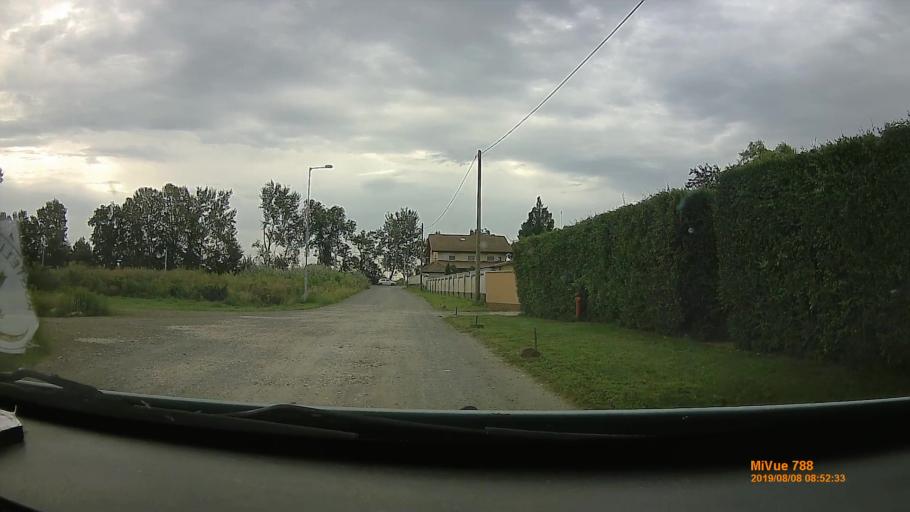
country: HU
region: Hajdu-Bihar
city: Debrecen
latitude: 47.5991
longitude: 21.6467
